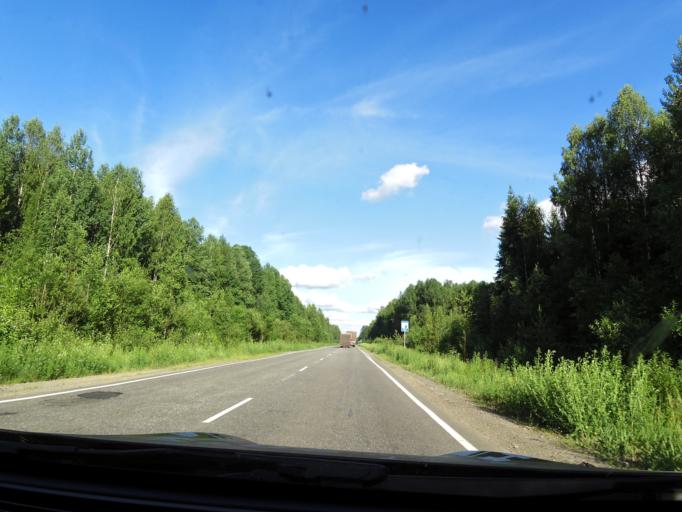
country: RU
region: Kirov
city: Omutninsk
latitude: 58.7697
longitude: 51.9607
